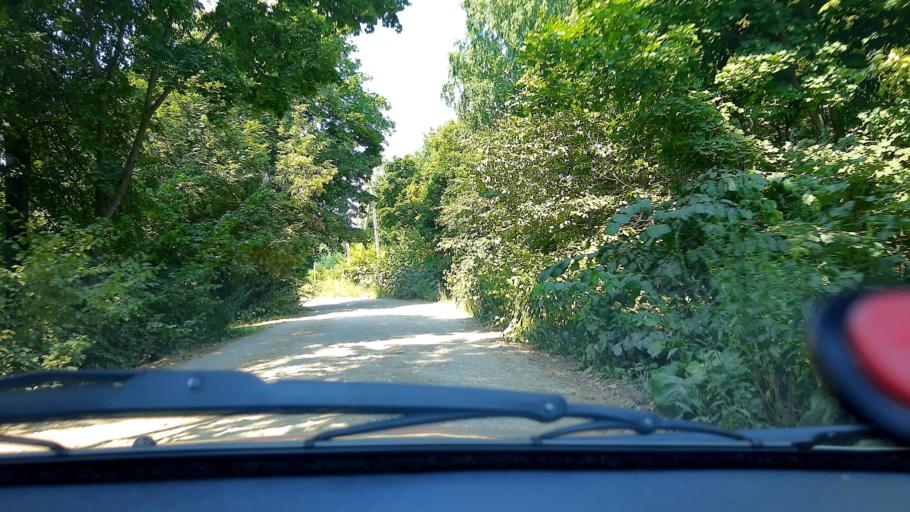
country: RU
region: Bashkortostan
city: Karmaskaly
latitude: 54.3877
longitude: 55.9023
